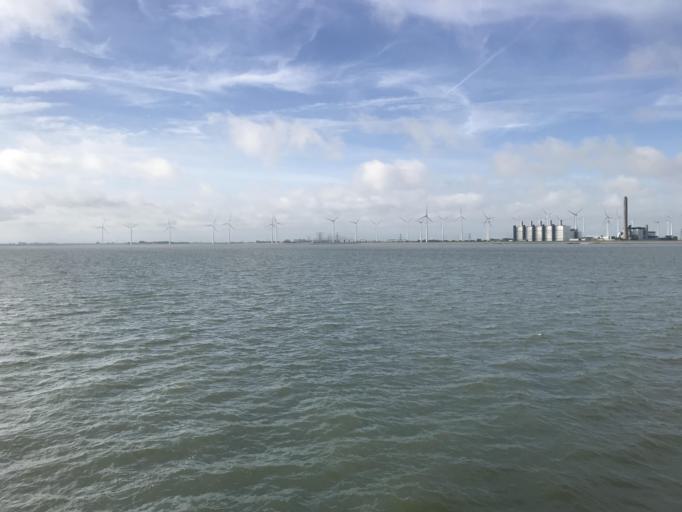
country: NL
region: Groningen
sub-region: Gemeente Delfzijl
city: Delfzijl
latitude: 53.4382
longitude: 6.9067
